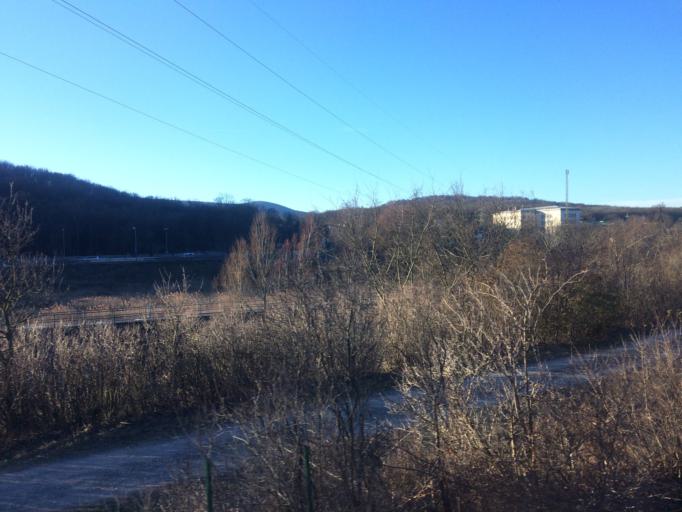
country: AT
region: Lower Austria
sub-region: Politischer Bezirk Wien-Umgebung
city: Purkersdorf
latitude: 48.2022
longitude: 16.2422
